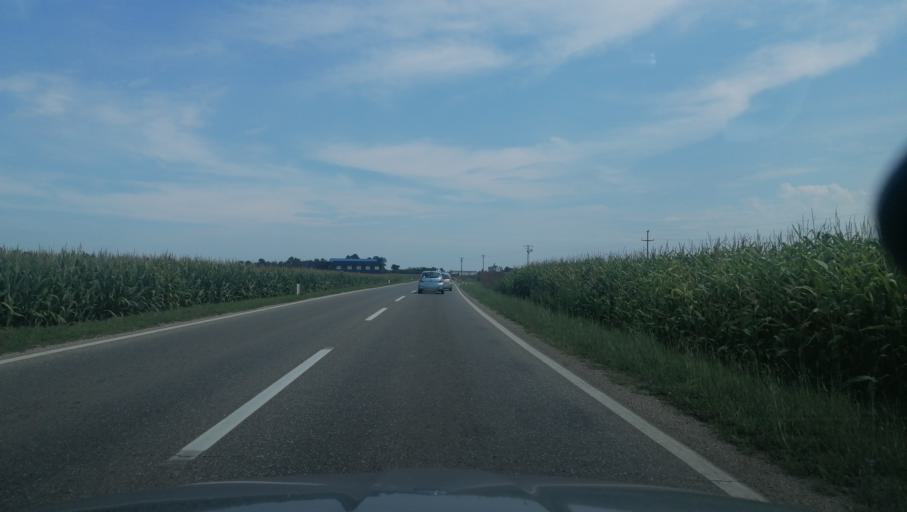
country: BA
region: Republika Srpska
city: Dvorovi
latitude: 44.7879
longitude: 19.2570
